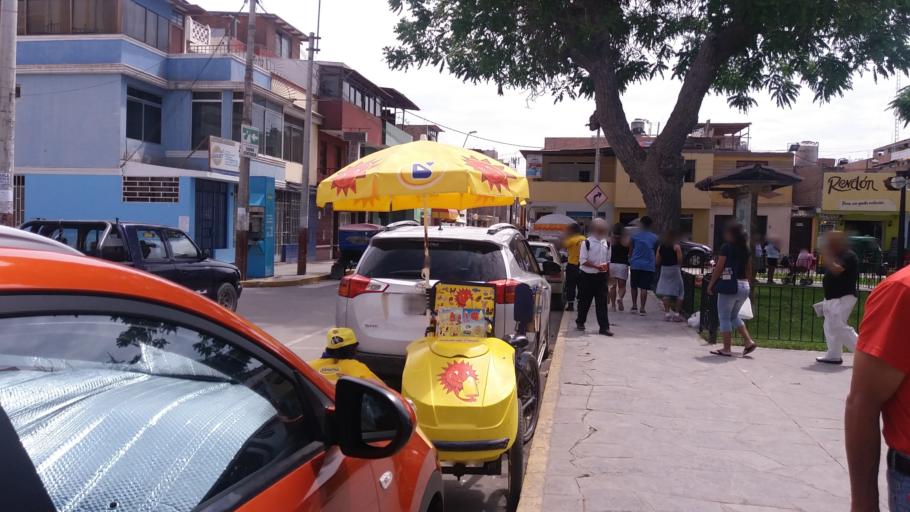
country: PE
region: Lima
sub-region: Lima
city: Punta Hermosa
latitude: -12.2735
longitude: -76.8687
